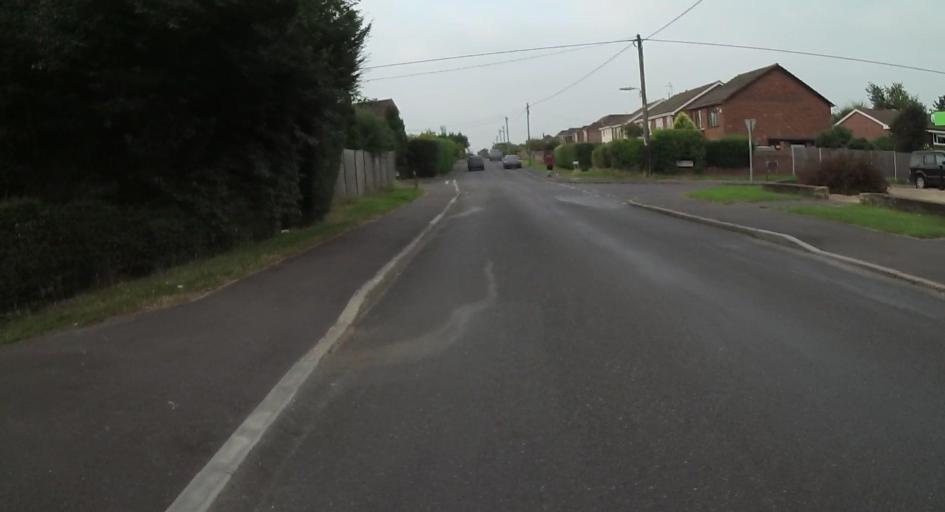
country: GB
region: England
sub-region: Hampshire
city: Old Basing
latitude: 51.2654
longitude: -1.0433
